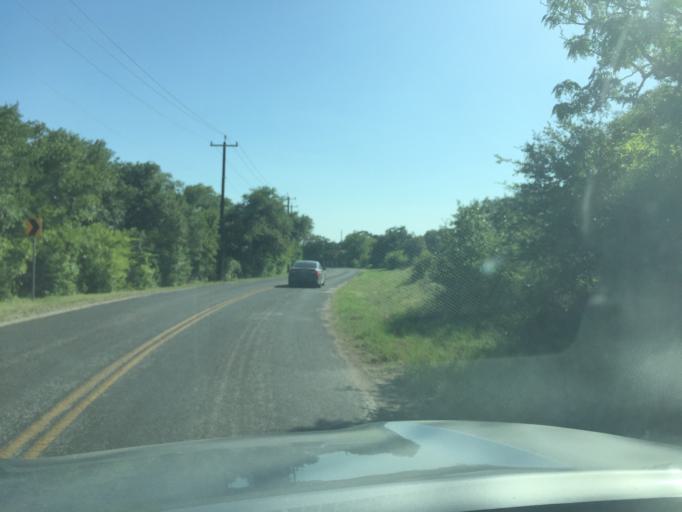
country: US
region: Texas
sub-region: Comal County
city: Bulverde
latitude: 29.7296
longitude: -98.4513
